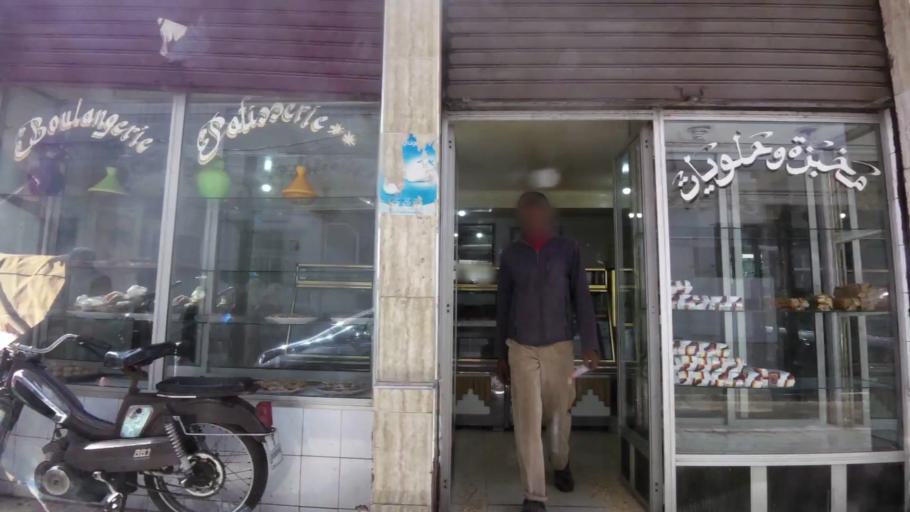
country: MA
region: Grand Casablanca
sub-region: Casablanca
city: Casablanca
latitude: 33.6015
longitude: -7.6198
